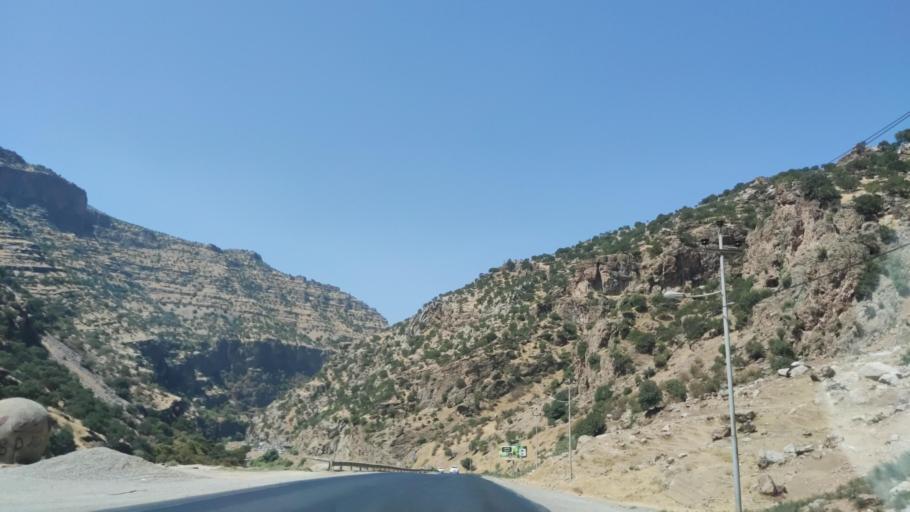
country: IQ
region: Arbil
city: Ruwandiz
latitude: 36.6311
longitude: 44.4771
